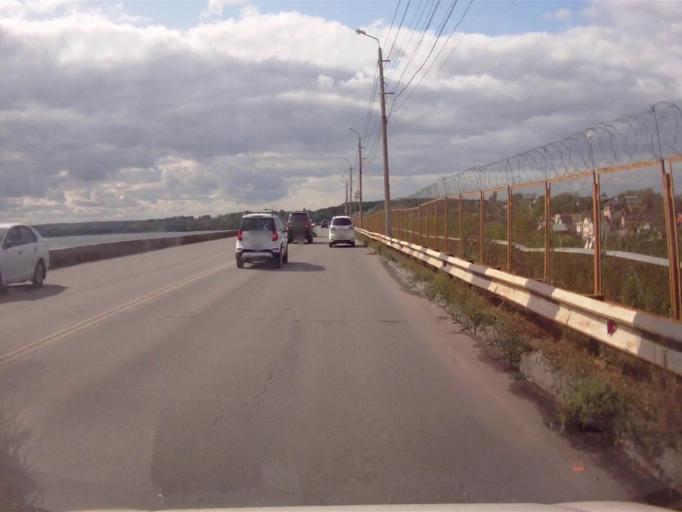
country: RU
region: Chelyabinsk
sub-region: Gorod Chelyabinsk
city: Chelyabinsk
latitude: 55.1462
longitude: 61.3121
